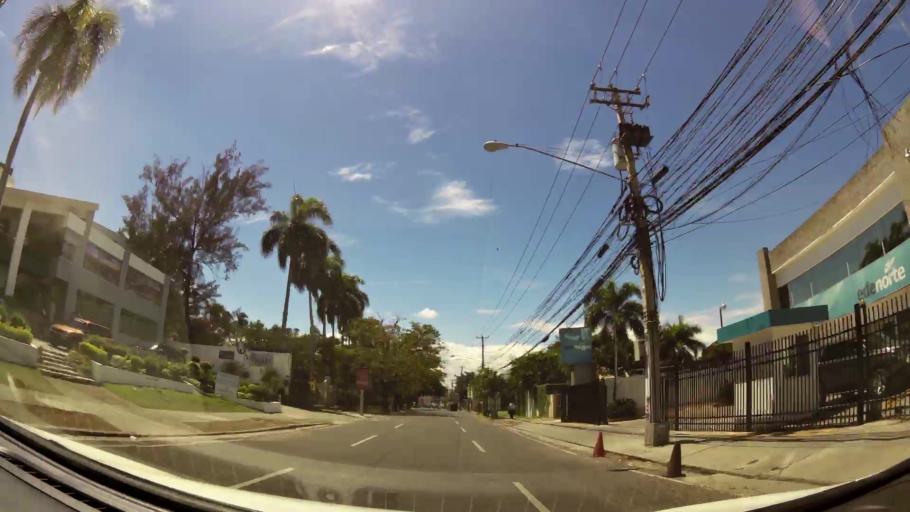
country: DO
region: Santiago
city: Santiago de los Caballeros
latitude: 19.4559
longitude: -70.6946
